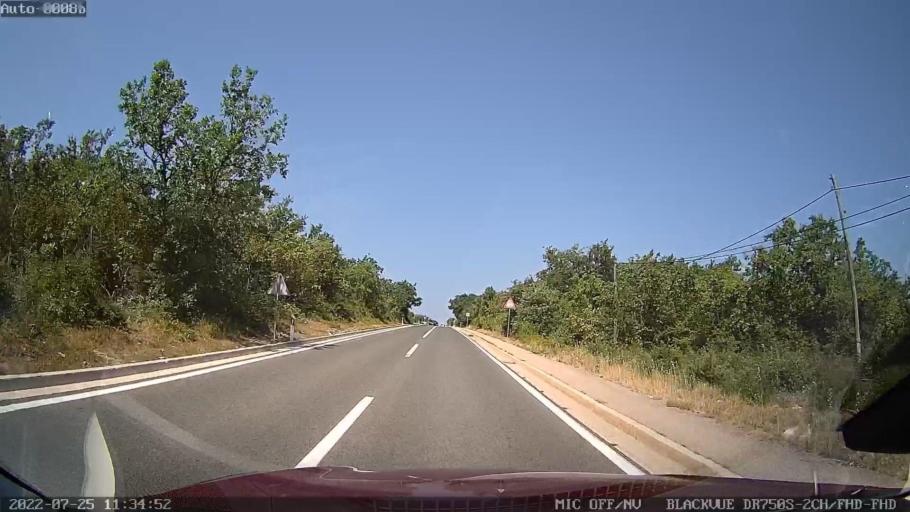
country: HR
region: Zadarska
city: Posedarje
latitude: 44.2314
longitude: 15.4165
